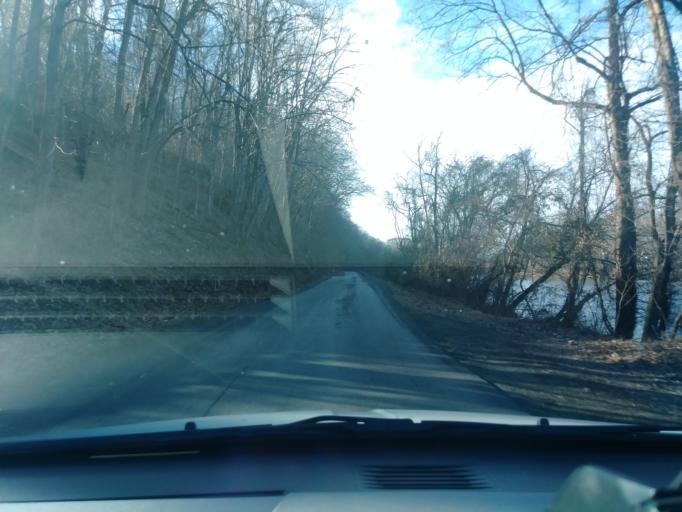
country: US
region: Tennessee
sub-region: Cocke County
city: Newport
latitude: 35.9783
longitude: -83.1519
